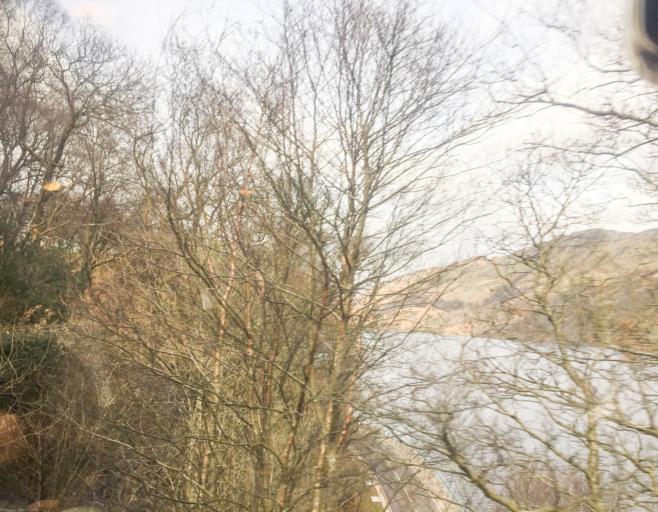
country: GB
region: Scotland
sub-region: Argyll and Bute
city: Garelochhead
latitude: 56.2850
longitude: -4.7047
